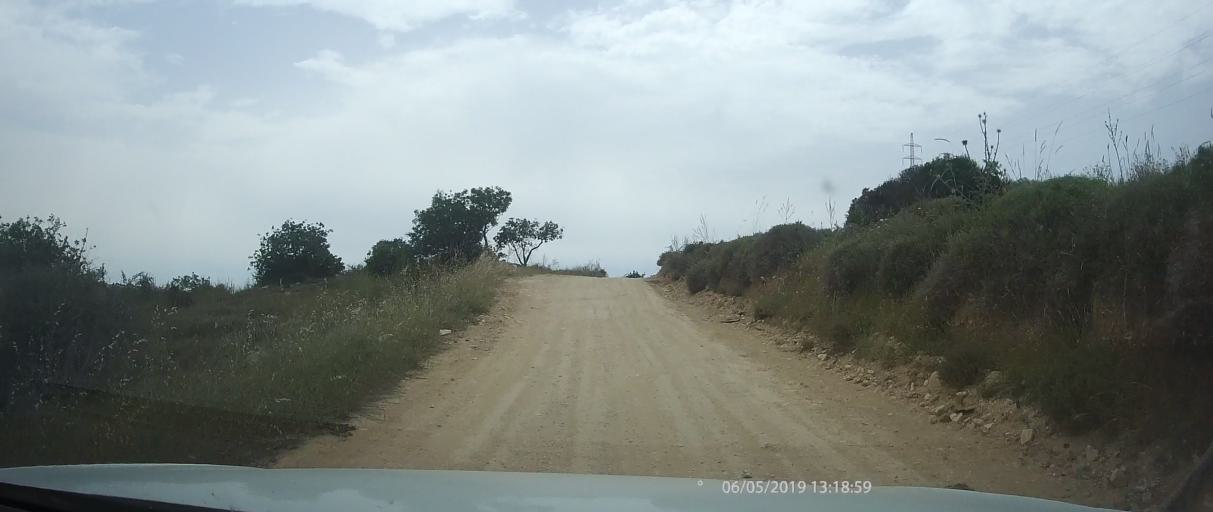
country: CY
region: Pafos
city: Tala
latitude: 34.8659
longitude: 32.4228
